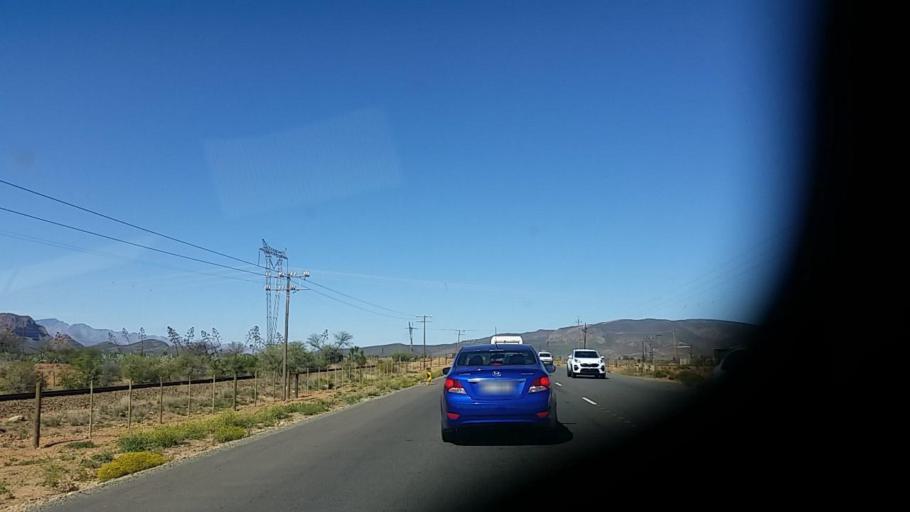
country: ZA
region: Western Cape
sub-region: Eden District Municipality
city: Oudtshoorn
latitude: -33.5610
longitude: 22.3936
